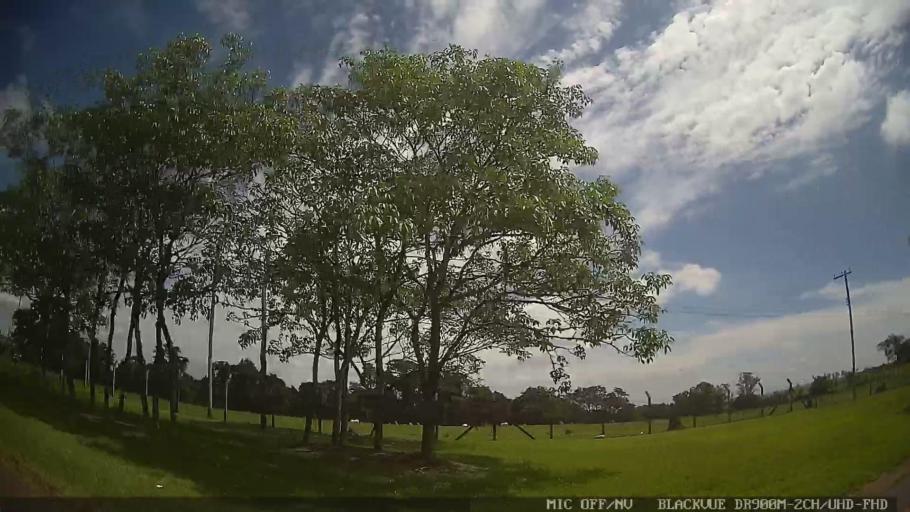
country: BR
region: Sao Paulo
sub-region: Laranjal Paulista
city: Laranjal Paulista
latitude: -23.0779
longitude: -47.8012
